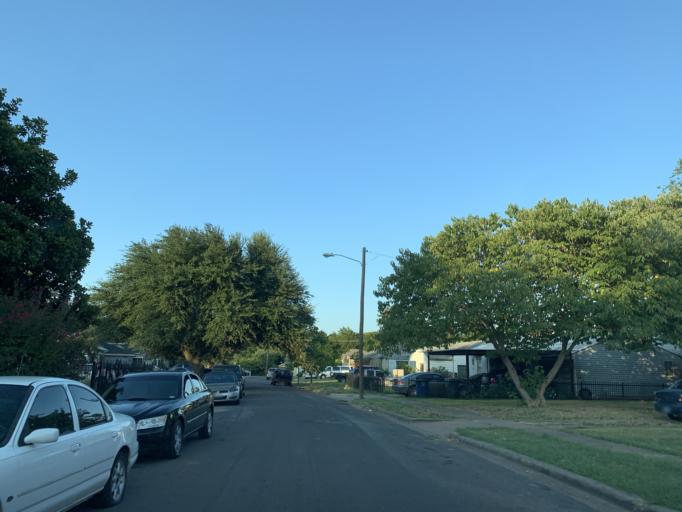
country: US
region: Texas
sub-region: Dallas County
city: Dallas
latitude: 32.7095
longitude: -96.7843
